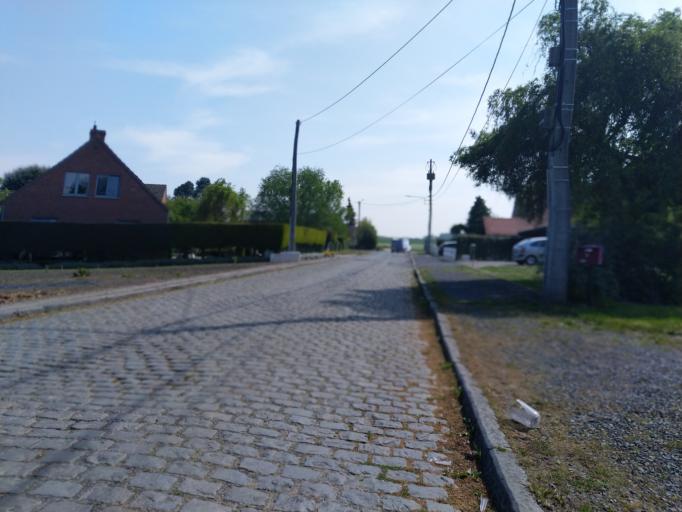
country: BE
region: Wallonia
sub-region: Province du Hainaut
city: Estinnes-au-Val
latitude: 50.4542
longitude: 4.0352
